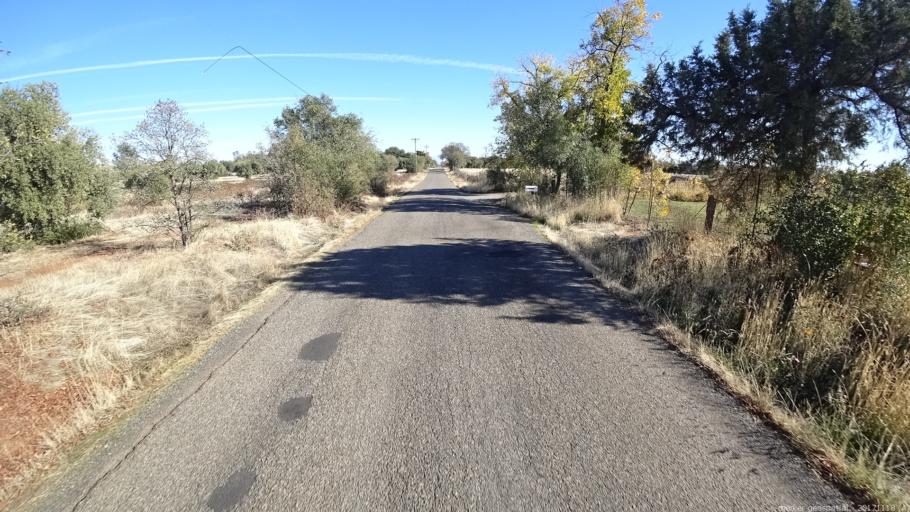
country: US
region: California
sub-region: Shasta County
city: Anderson
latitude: 40.4392
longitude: -122.4285
